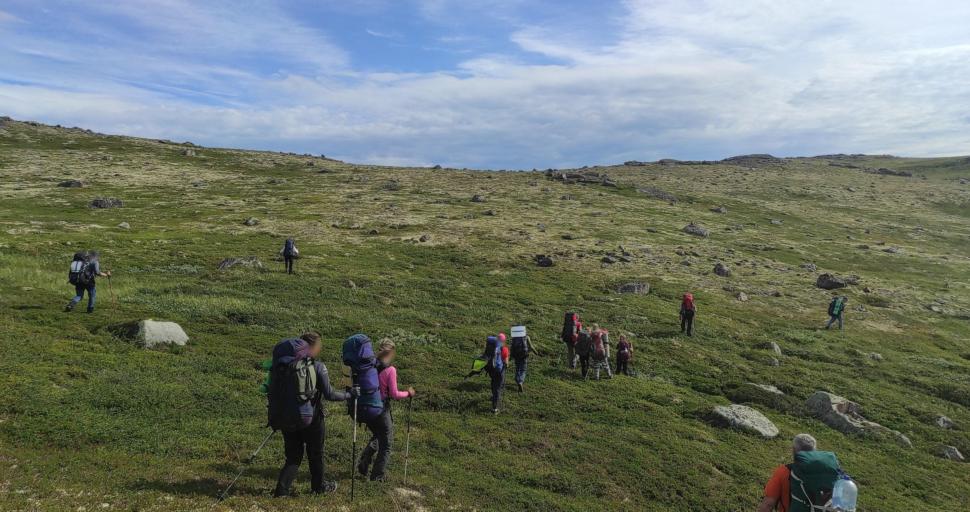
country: RU
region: Murmansk
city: Teriberka
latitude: 69.1701
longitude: 35.5948
